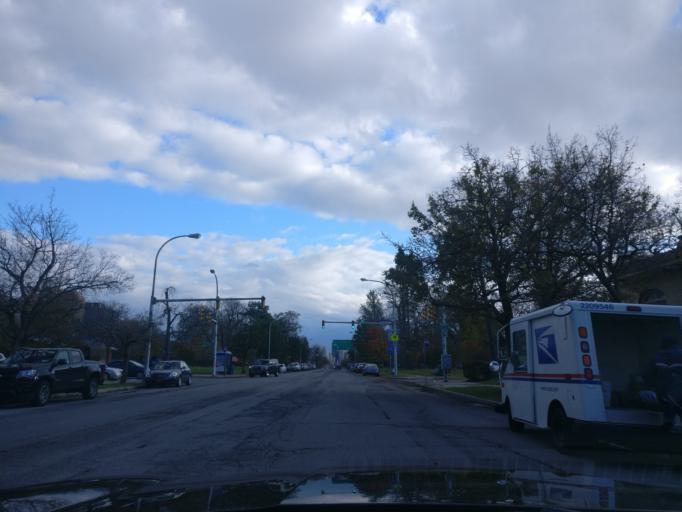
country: US
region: New York
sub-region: Erie County
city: Buffalo
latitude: 42.9032
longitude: -78.8940
